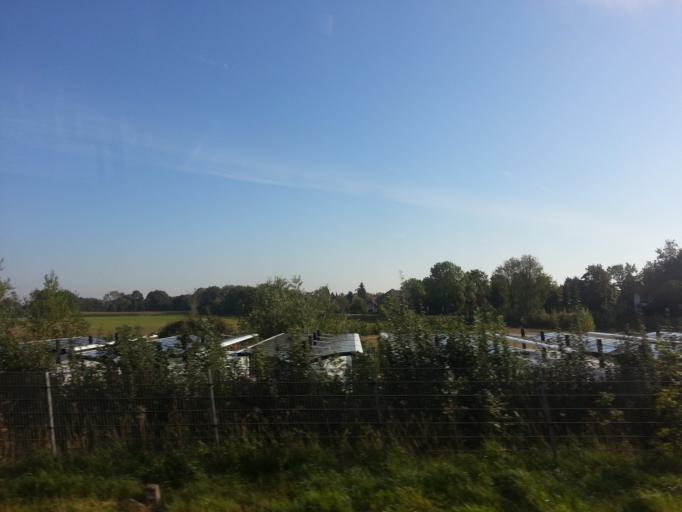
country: NL
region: Gelderland
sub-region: Gemeente Geldermalsen
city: Geldermalsen
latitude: 51.8834
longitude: 5.2713
